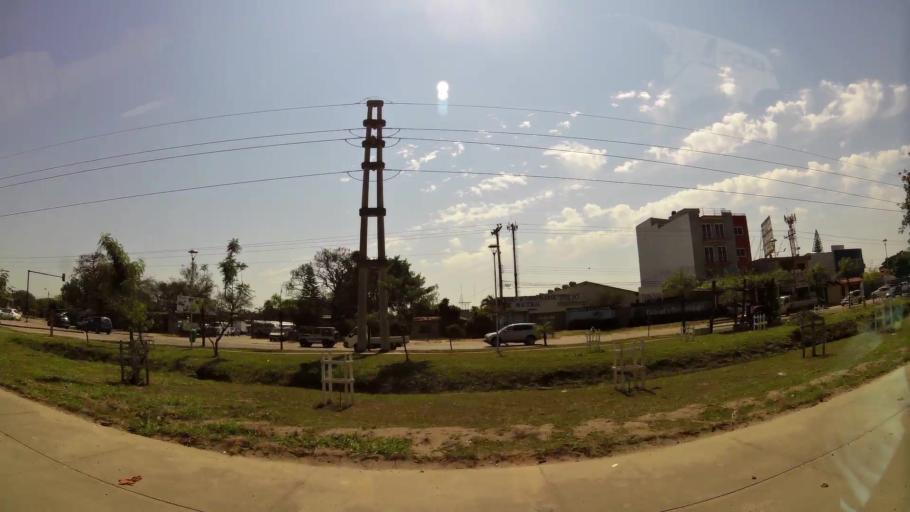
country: BO
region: Santa Cruz
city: Santa Cruz de la Sierra
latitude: -17.7517
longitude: -63.1908
